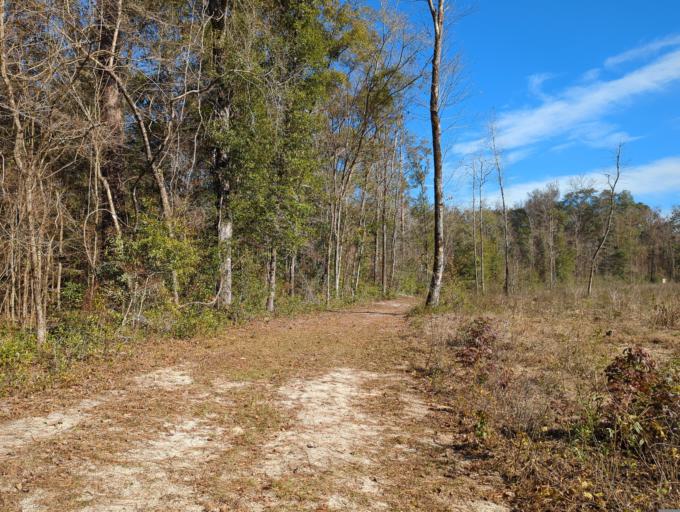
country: US
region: Florida
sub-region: Wakulla County
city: Crawfordville
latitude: 30.1879
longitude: -84.3275
